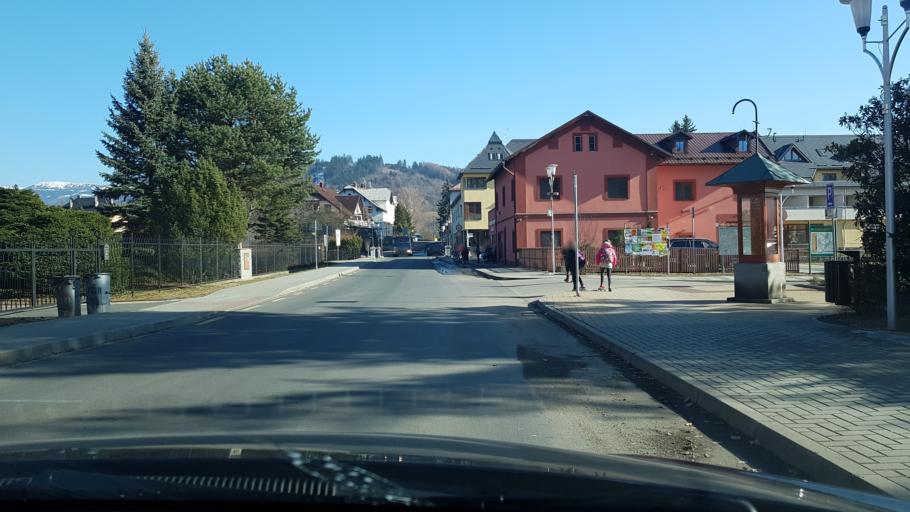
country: CZ
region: Olomoucky
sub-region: Okres Sumperk
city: Velke Losiny
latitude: 50.0326
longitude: 17.0387
